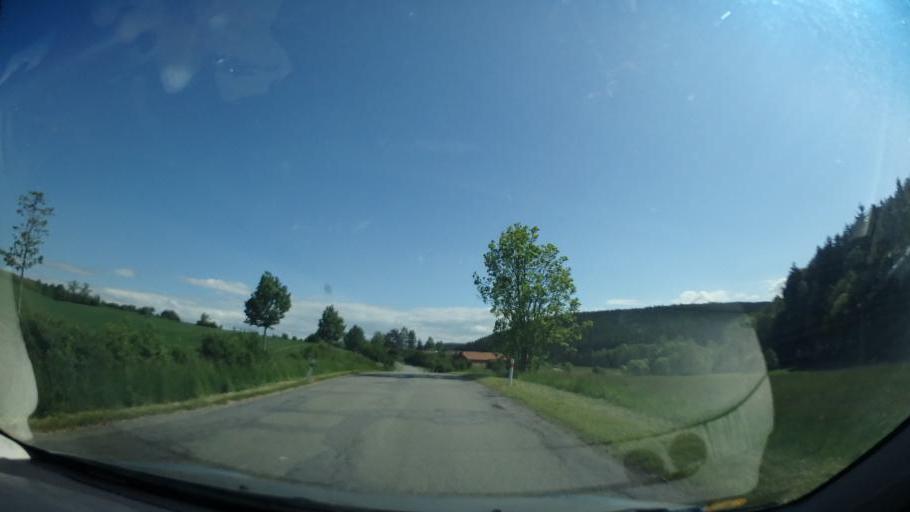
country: CZ
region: South Moravian
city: Velke Opatovice
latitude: 49.6442
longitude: 16.6155
